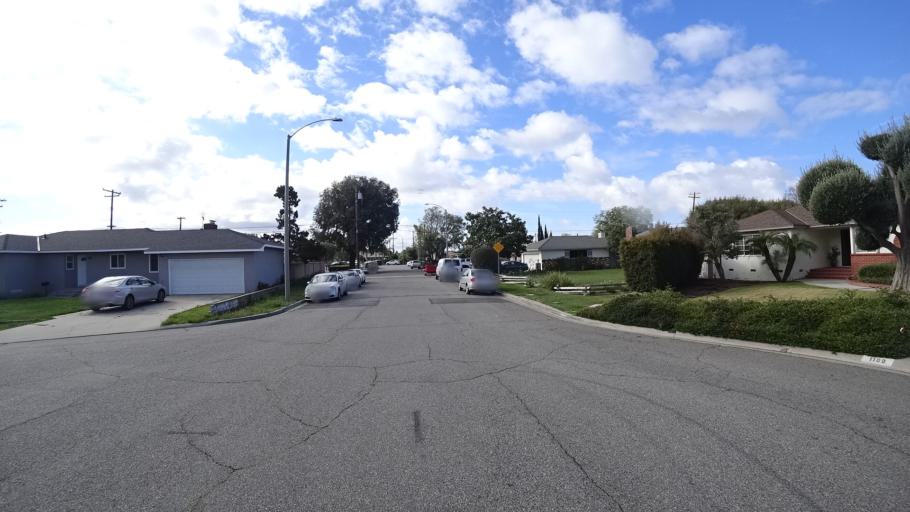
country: US
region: California
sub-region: Orange County
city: Anaheim
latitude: 33.8495
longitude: -117.9001
